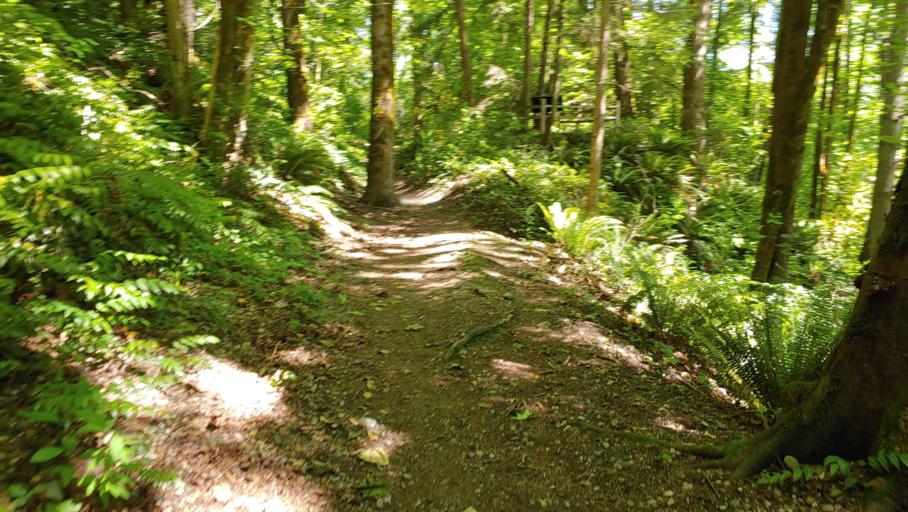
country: US
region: Washington
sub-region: King County
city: Newcastle
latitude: 47.5182
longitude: -122.1840
